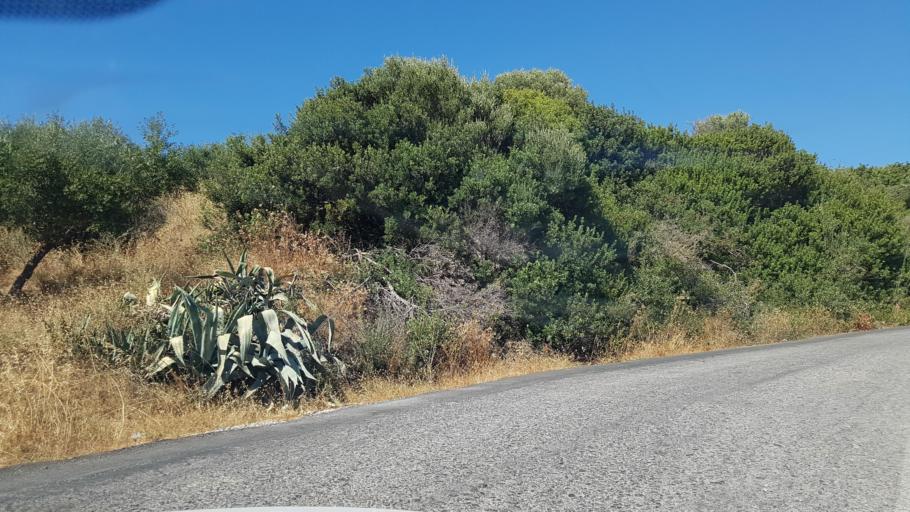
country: GR
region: Crete
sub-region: Nomos Chanias
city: Kissamos
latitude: 35.4967
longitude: 23.7210
